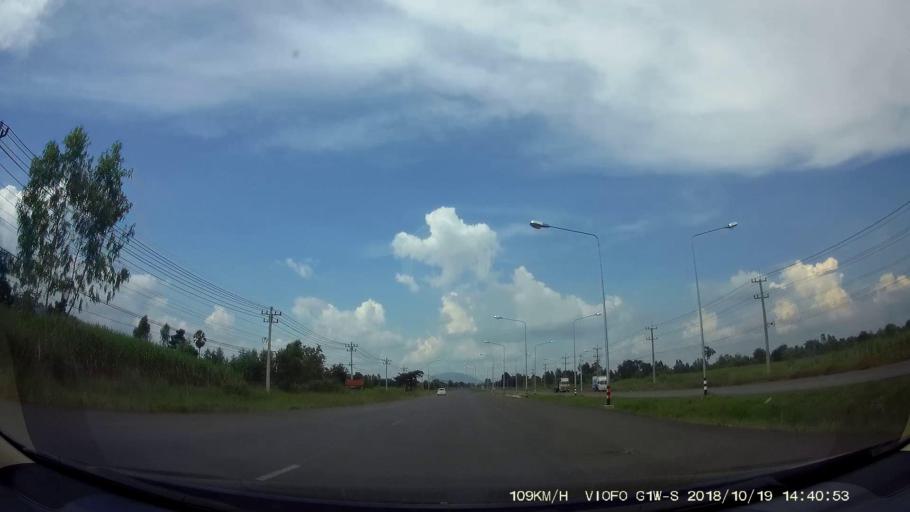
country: TH
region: Chaiyaphum
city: Phu Khiao
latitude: 16.2477
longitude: 102.1973
